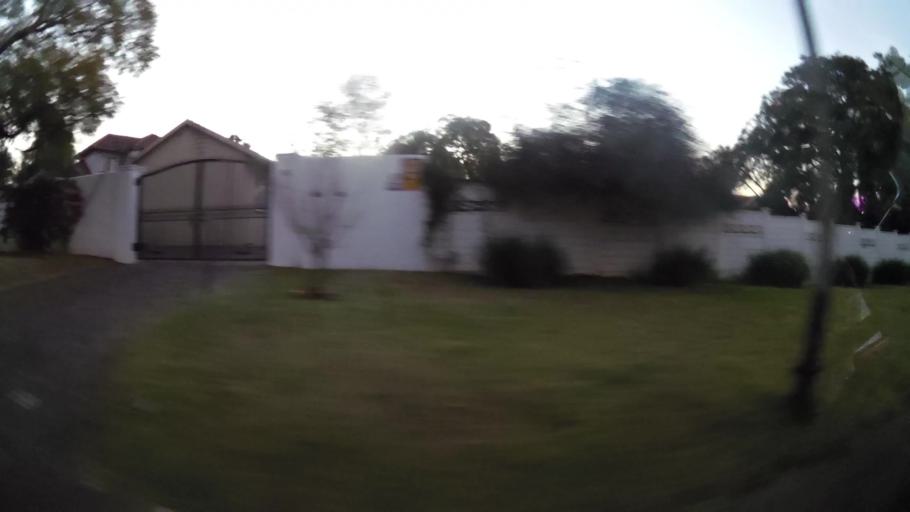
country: ZA
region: Gauteng
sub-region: City of Johannesburg Metropolitan Municipality
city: Johannesburg
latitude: -26.1409
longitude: 28.0010
